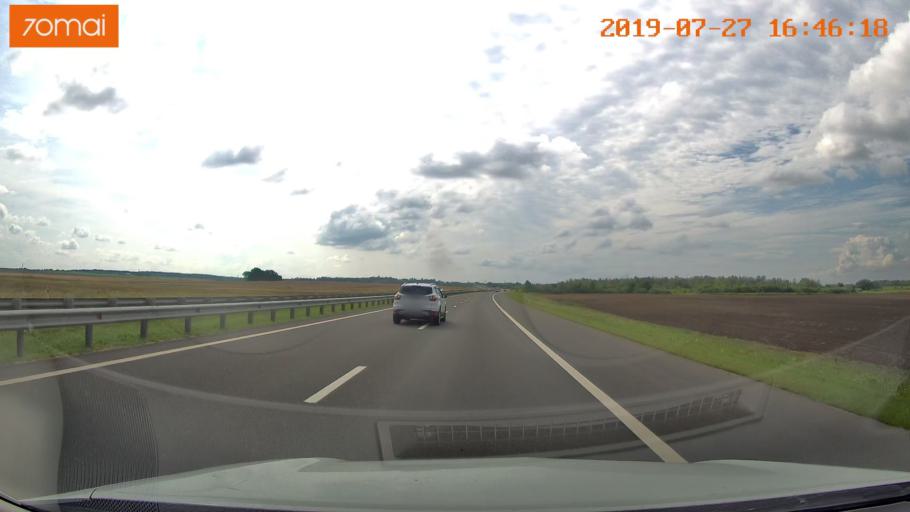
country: RU
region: Kaliningrad
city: Gvardeysk
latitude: 54.6673
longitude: 21.0255
